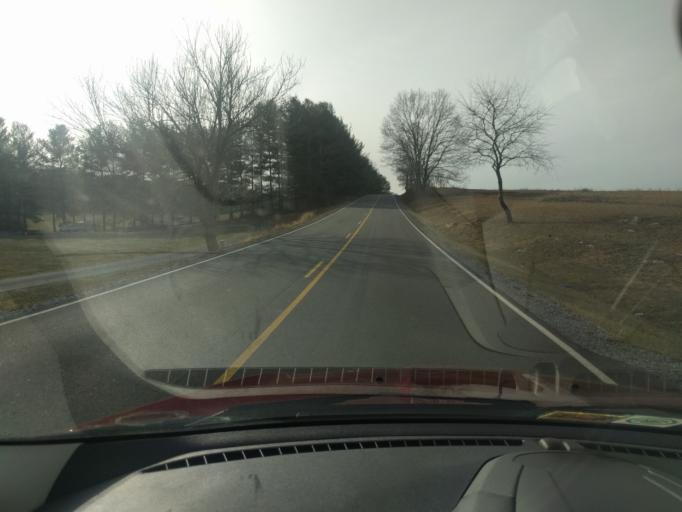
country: US
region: Virginia
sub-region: Augusta County
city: Stuarts Draft
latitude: 38.0351
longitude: -79.1151
